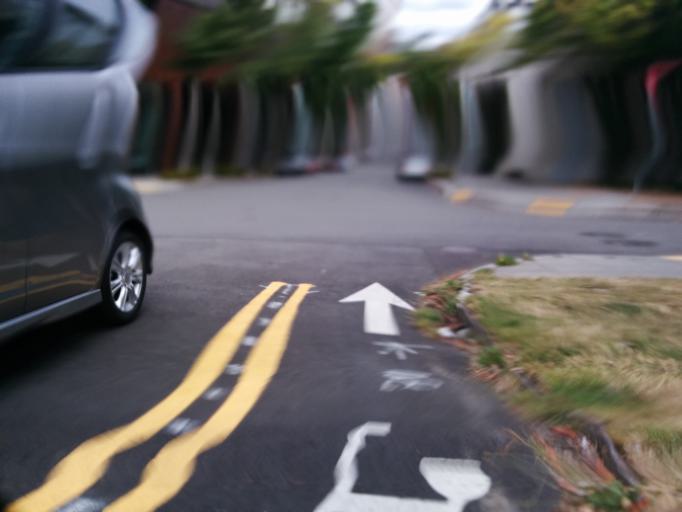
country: US
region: Washington
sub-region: King County
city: Seattle
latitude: 47.6568
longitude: -122.3170
